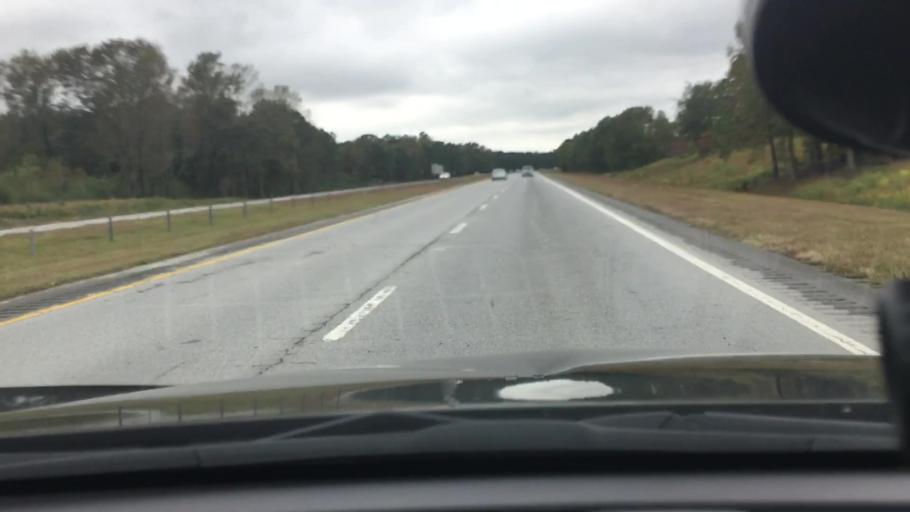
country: US
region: North Carolina
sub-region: Pitt County
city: Farmville
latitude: 35.6202
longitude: -77.6954
